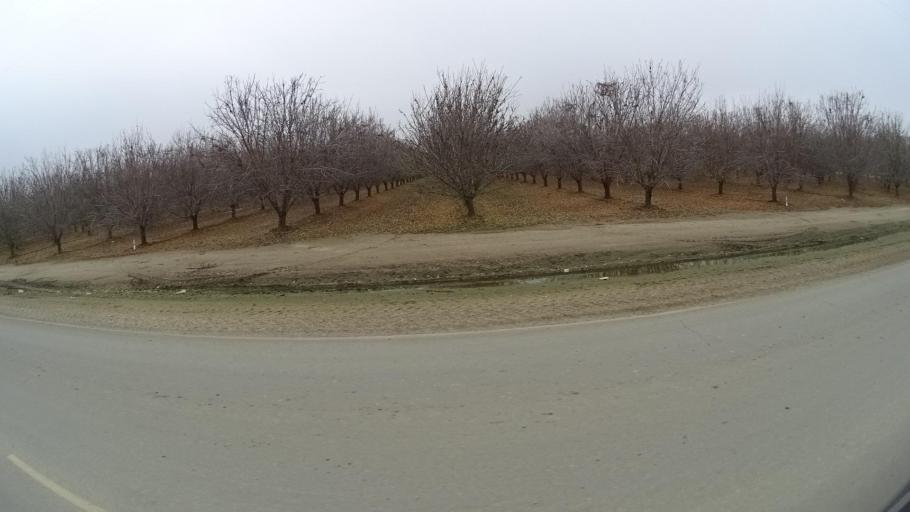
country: US
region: California
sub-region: Kern County
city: Greenfield
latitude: 35.2380
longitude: -119.0617
